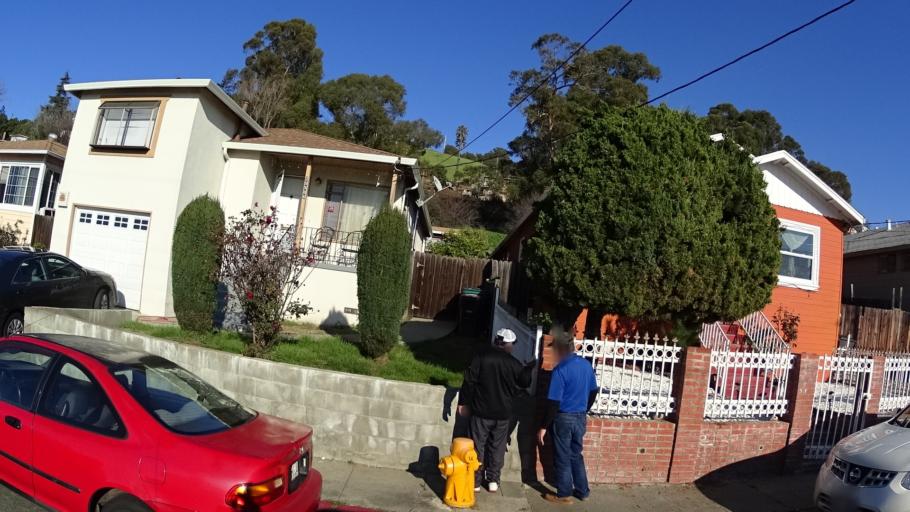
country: US
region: California
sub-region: Alameda County
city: Hayward
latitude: 37.6564
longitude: -122.0689
